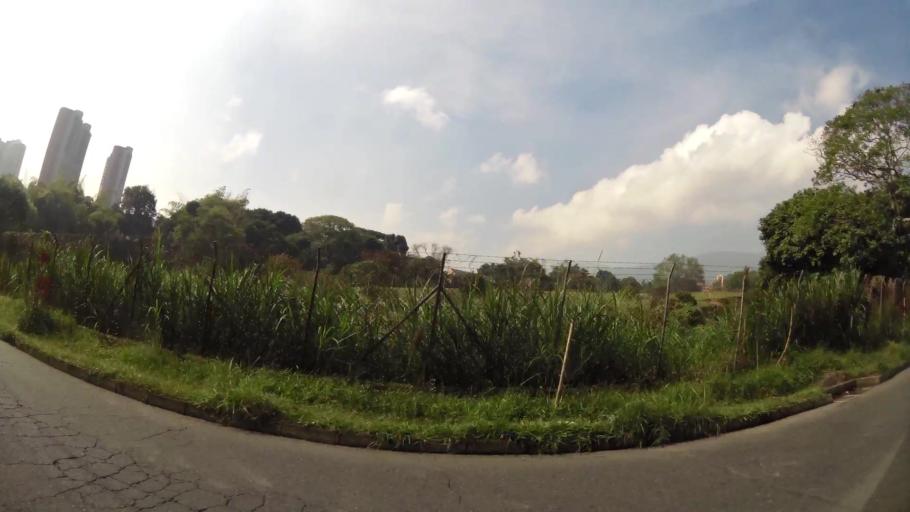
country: CO
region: Antioquia
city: La Estrella
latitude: 6.1687
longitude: -75.6366
